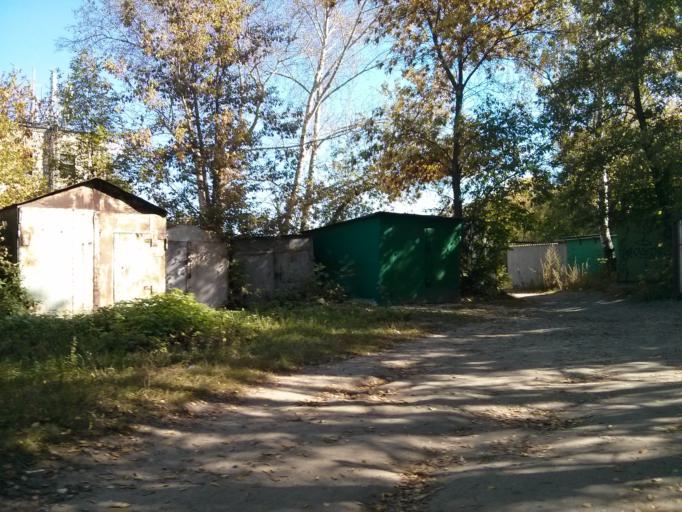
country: RU
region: Vladimir
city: Murom
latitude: 55.5507
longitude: 42.0572
